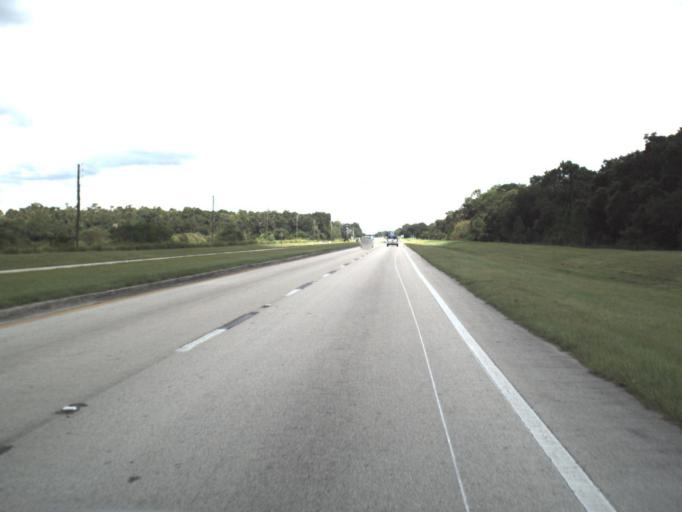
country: US
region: Florida
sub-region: Polk County
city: Fussels Corner
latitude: 28.0100
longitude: -81.8376
